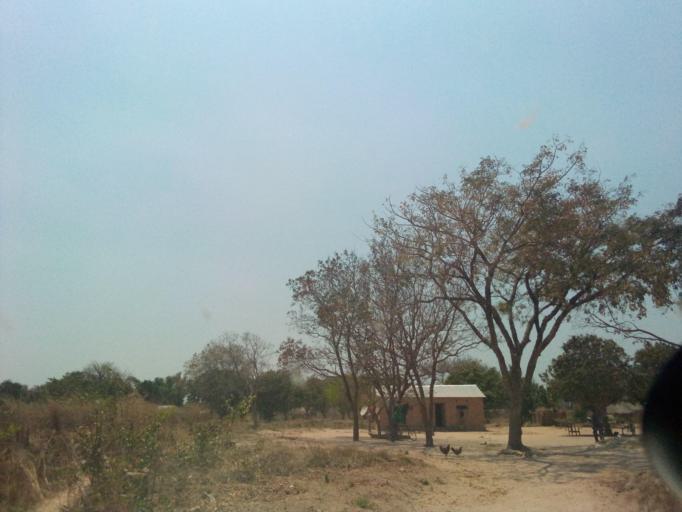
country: ZM
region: Copperbelt
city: Kataba
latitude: -12.2368
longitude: 30.3133
